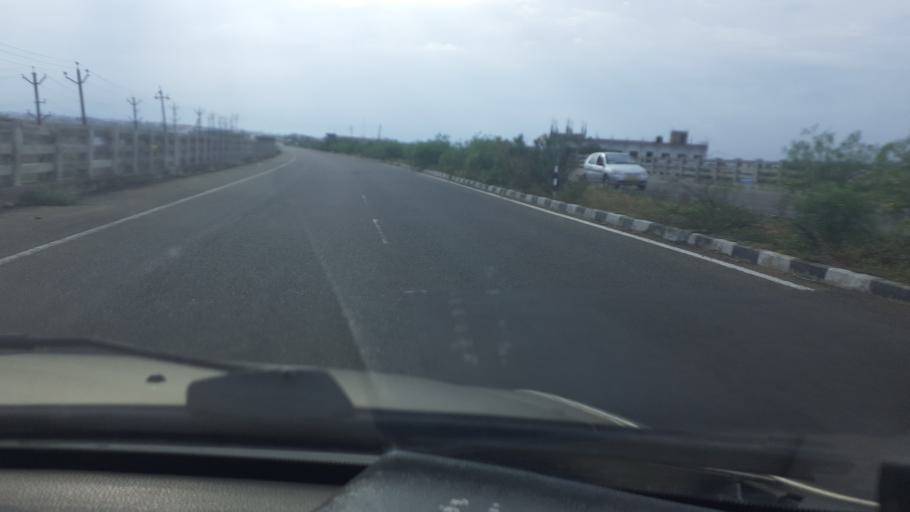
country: IN
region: Tamil Nadu
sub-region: Tirunelveli Kattabo
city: Tirunelveli
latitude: 8.6659
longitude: 77.7375
